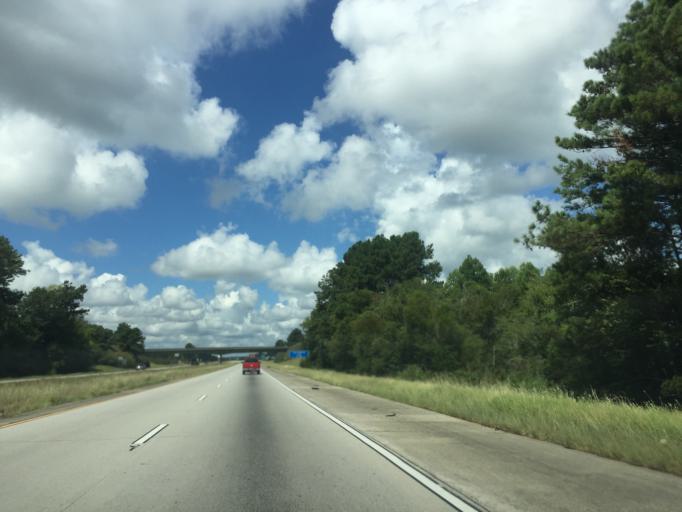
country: US
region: Georgia
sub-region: Candler County
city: Metter
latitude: 32.3739
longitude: -82.0520
